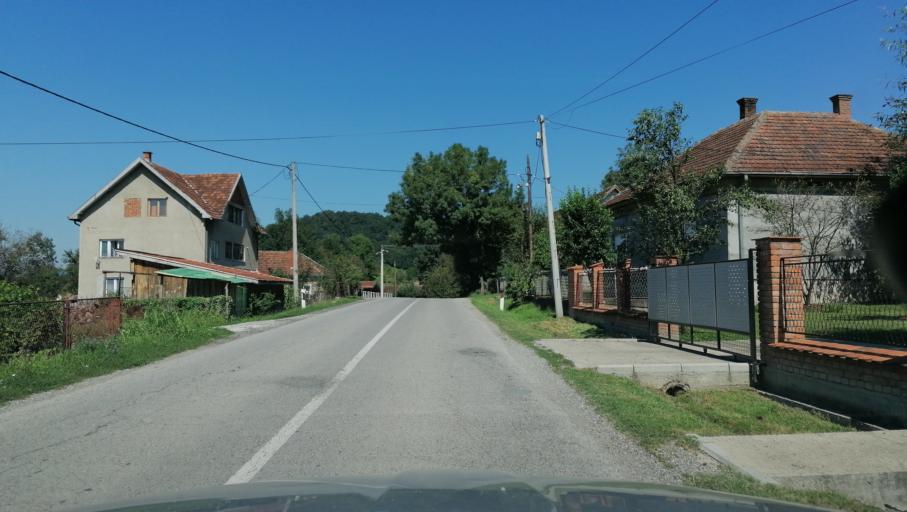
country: RS
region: Central Serbia
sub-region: Raski Okrug
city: Vrnjacka Banja
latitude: 43.7027
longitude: 20.8530
